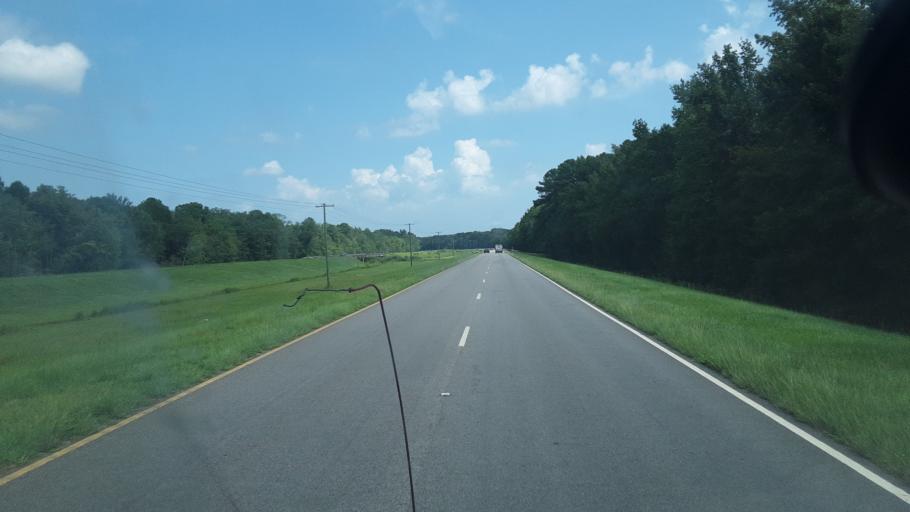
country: US
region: South Carolina
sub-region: Bamberg County
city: Bamberg
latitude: 33.3283
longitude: -81.0239
